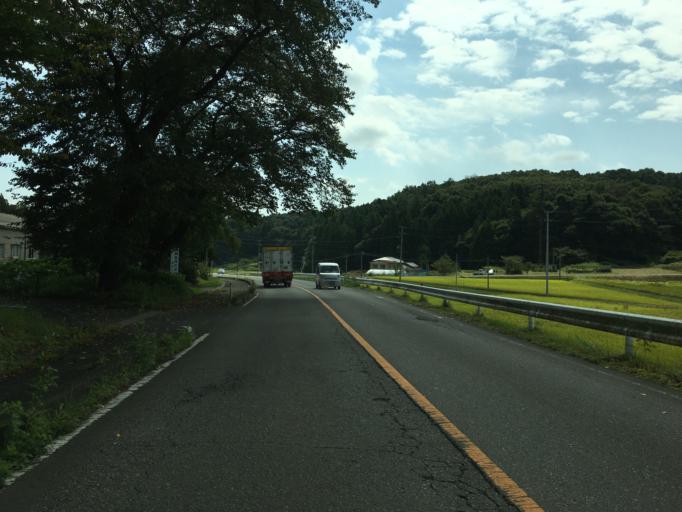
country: JP
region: Fukushima
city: Nihommatsu
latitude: 37.5984
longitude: 140.3992
